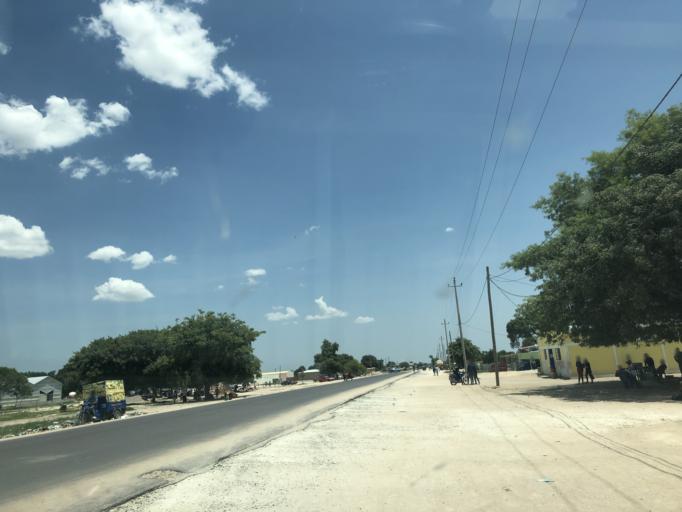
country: AO
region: Cunene
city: Ondjiva
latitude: -17.0371
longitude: 15.7494
